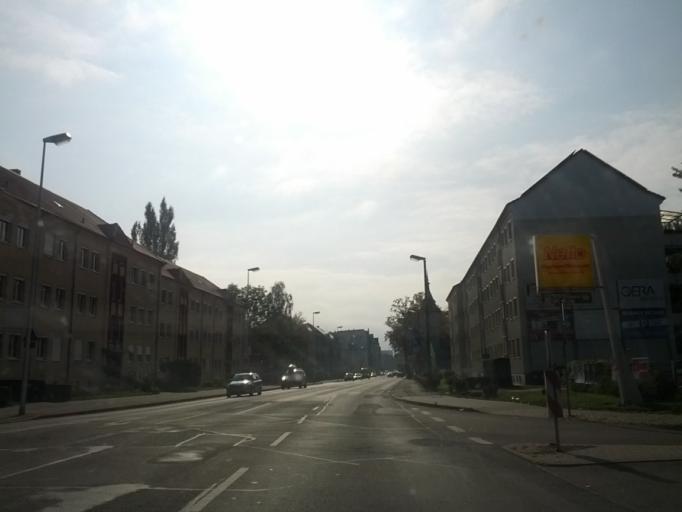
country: DE
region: Thuringia
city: Gera
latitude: 50.8878
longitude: 12.0739
